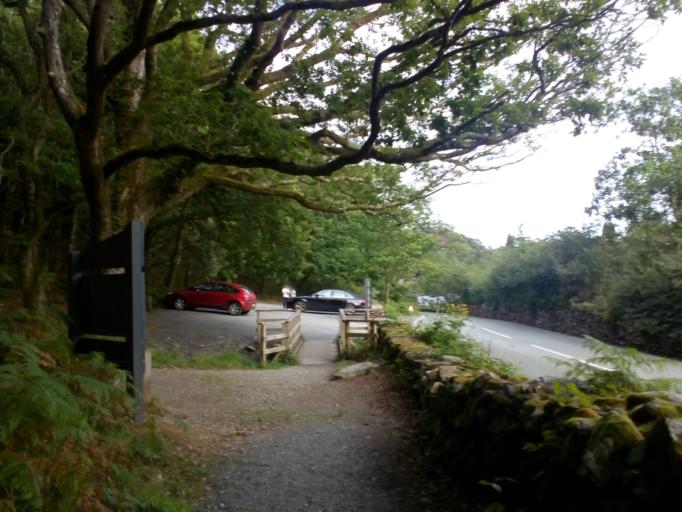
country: GB
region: Wales
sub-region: Gwynedd
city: Maentwrog
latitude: 52.9527
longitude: -4.0084
